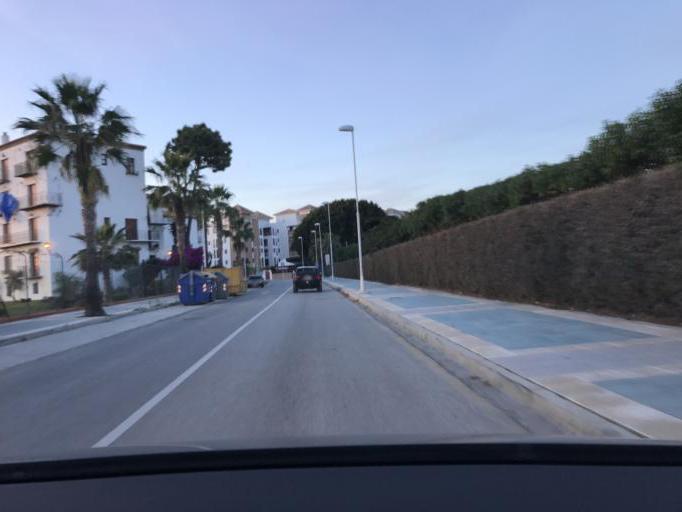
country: ES
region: Andalusia
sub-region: Provincia de Granada
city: El Varadero
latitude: 36.7185
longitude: -3.5584
